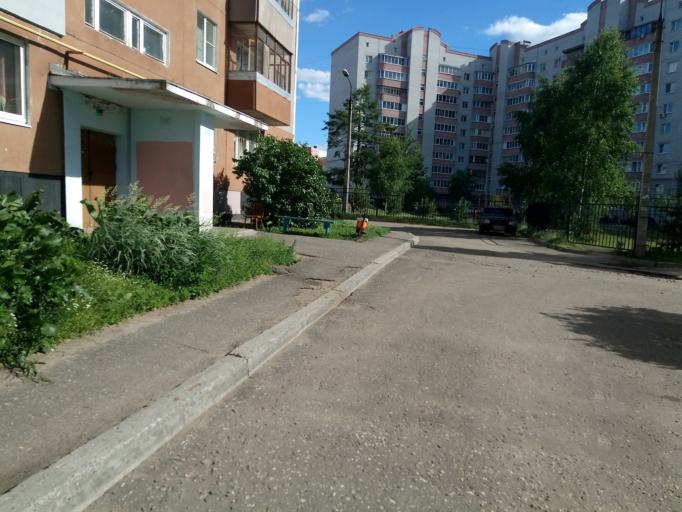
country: RU
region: Jaroslavl
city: Yaroslavl
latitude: 57.6397
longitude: 39.9500
